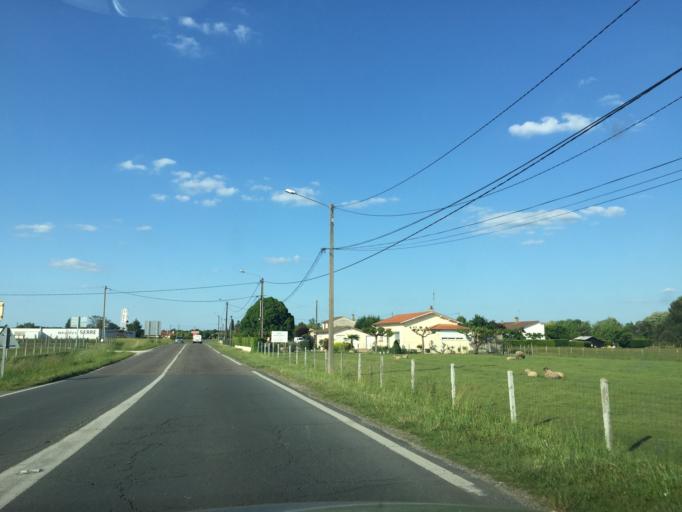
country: FR
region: Aquitaine
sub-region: Departement de la Gironde
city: Les Peintures
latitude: 45.0533
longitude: -0.1110
